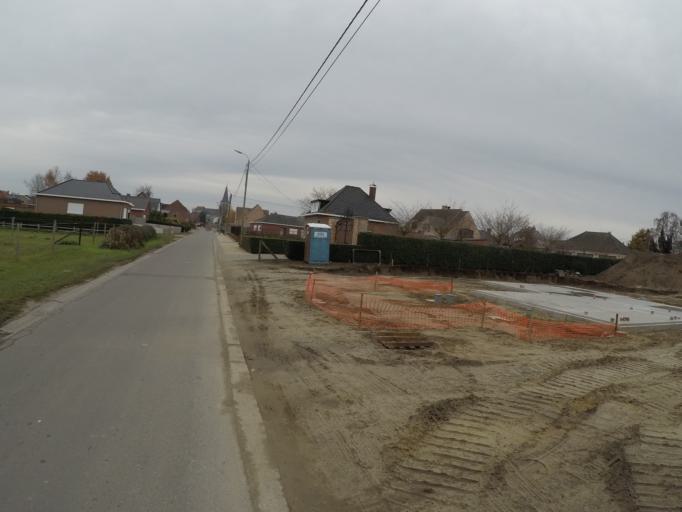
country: BE
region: Flanders
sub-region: Provincie Antwerpen
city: Heist-op-den-Berg
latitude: 51.0876
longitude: 4.7267
